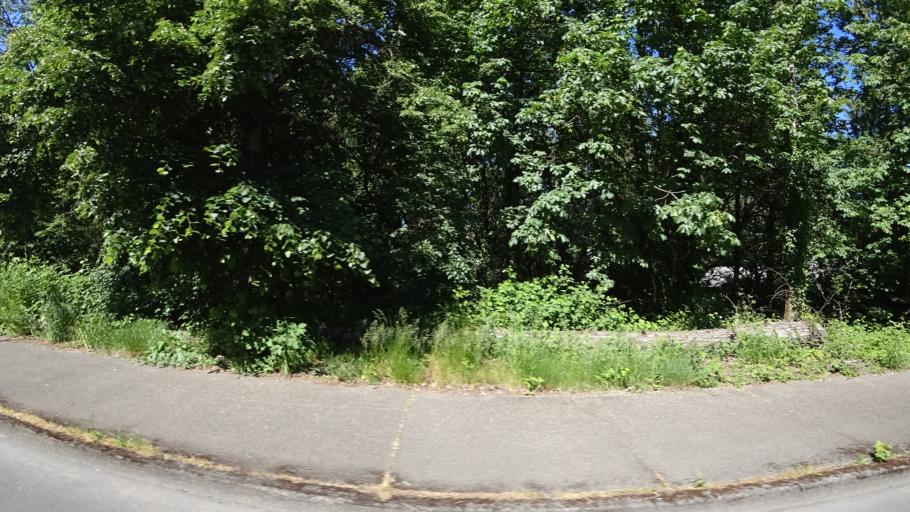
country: US
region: Oregon
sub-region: Multnomah County
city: Gresham
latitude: 45.4860
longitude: -122.4737
